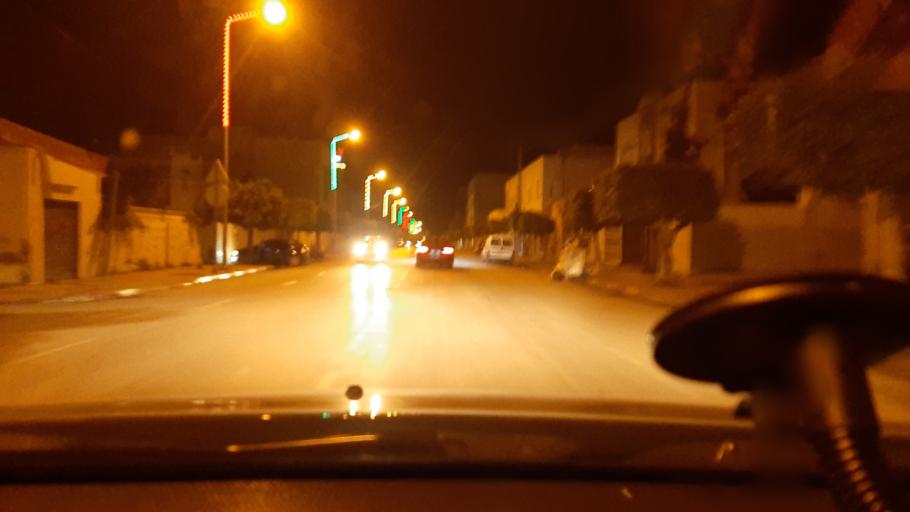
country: TN
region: Safaqis
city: Sfax
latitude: 34.7781
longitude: 10.7261
